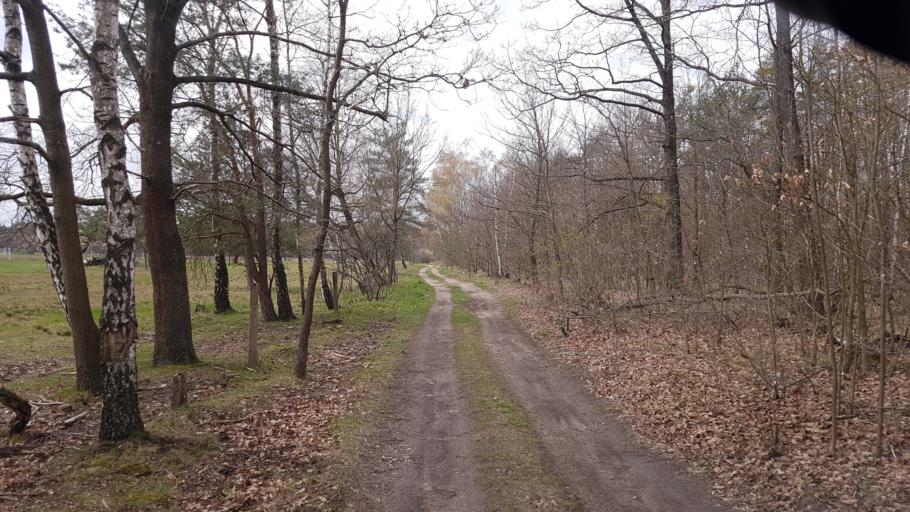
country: DE
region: Brandenburg
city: Hohenleipisch
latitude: 51.5071
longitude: 13.5493
